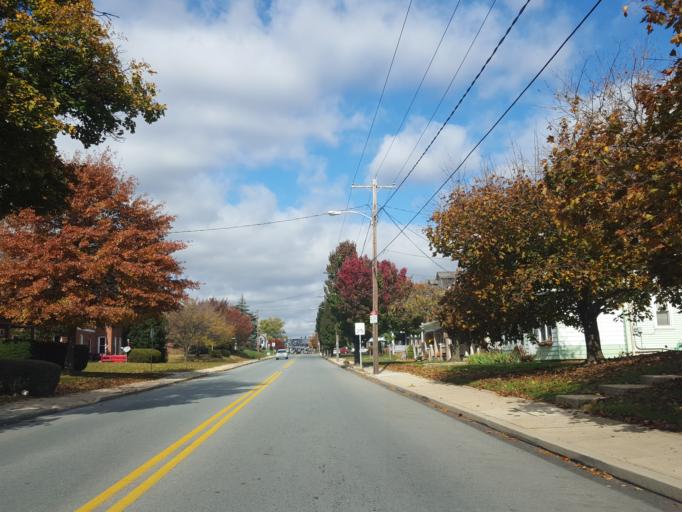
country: US
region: Pennsylvania
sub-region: York County
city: Red Lion
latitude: 39.8942
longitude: -76.5991
